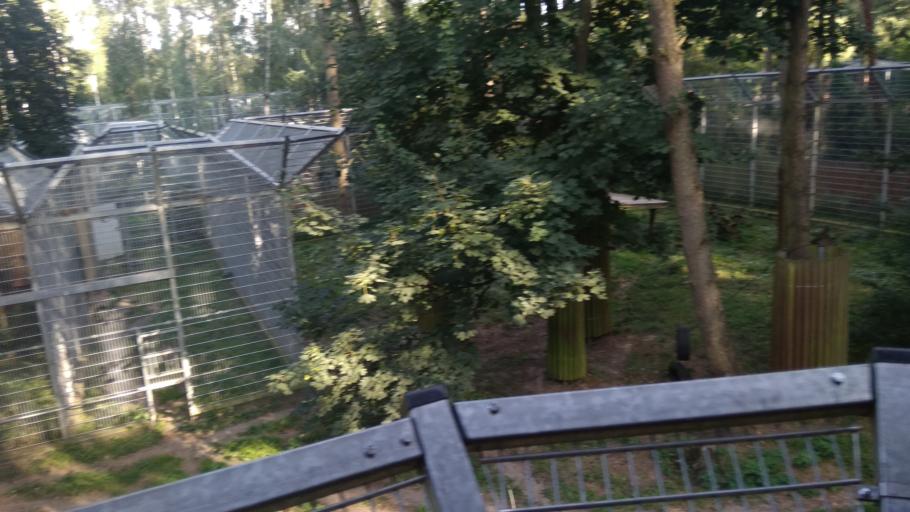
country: PL
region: Kujawsko-Pomorskie
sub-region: Bydgoszcz
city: Bydgoszcz
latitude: 53.1627
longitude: 18.0352
